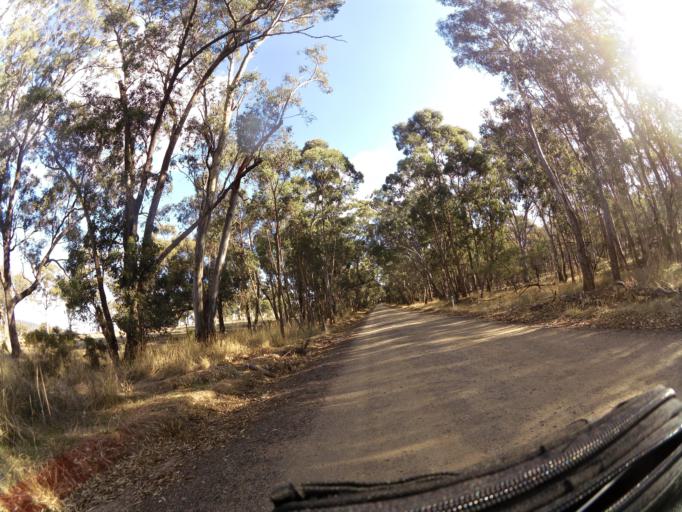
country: AU
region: Victoria
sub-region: Greater Bendigo
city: Kennington
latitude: -37.0178
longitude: 144.8068
